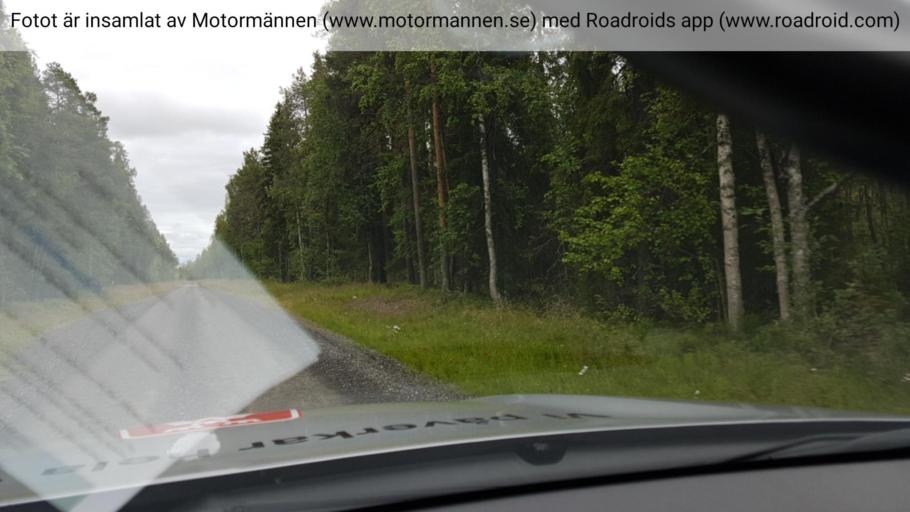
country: SE
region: Norrbotten
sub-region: Pajala Kommun
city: Pajala
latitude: 67.0950
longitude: 22.7388
